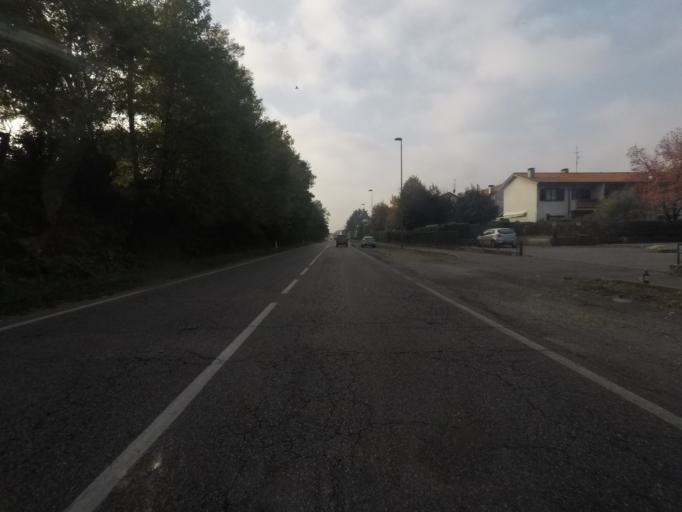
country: IT
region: Lombardy
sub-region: Provincia di Monza e Brianza
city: Villanova
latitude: 45.6273
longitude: 9.3898
